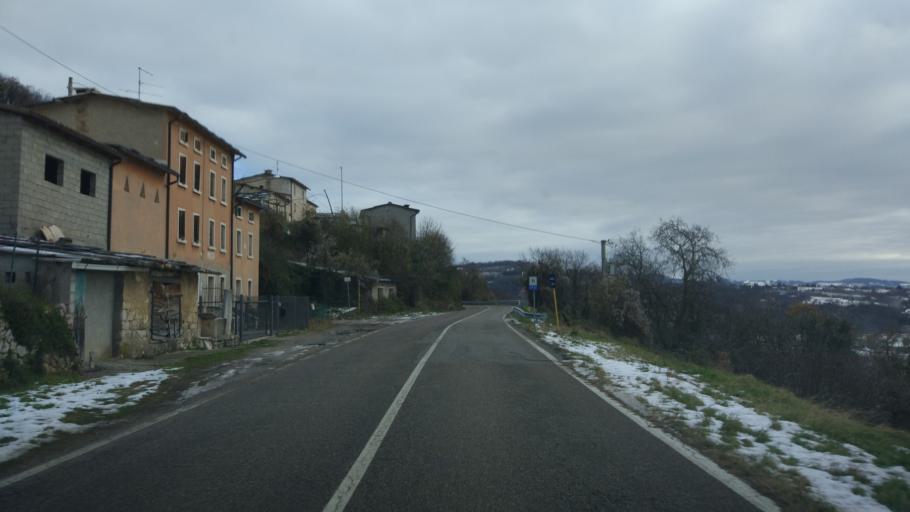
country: IT
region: Veneto
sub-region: Provincia di Verona
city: Marano di Valpolicella
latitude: 45.5760
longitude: 10.9338
